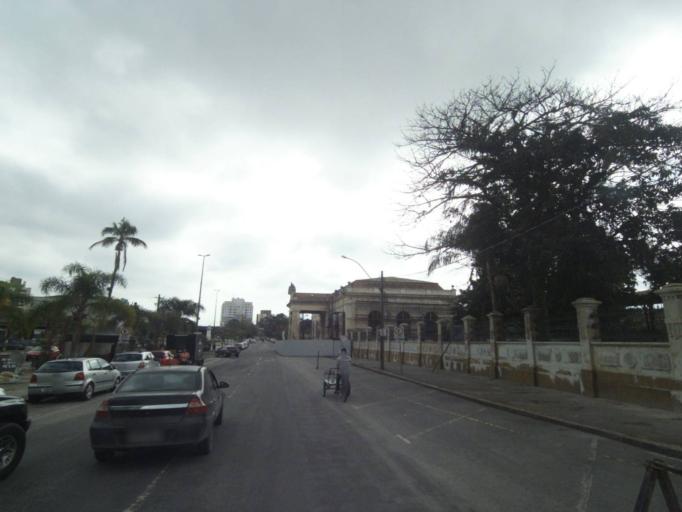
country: BR
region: Parana
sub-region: Paranagua
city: Paranagua
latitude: -25.5173
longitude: -48.5062
